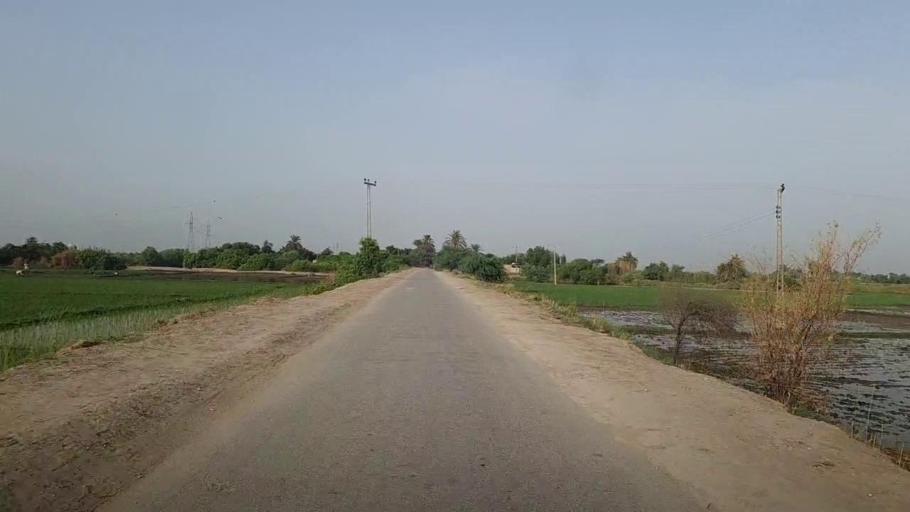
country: PK
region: Sindh
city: Mehar
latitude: 27.1499
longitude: 67.8002
